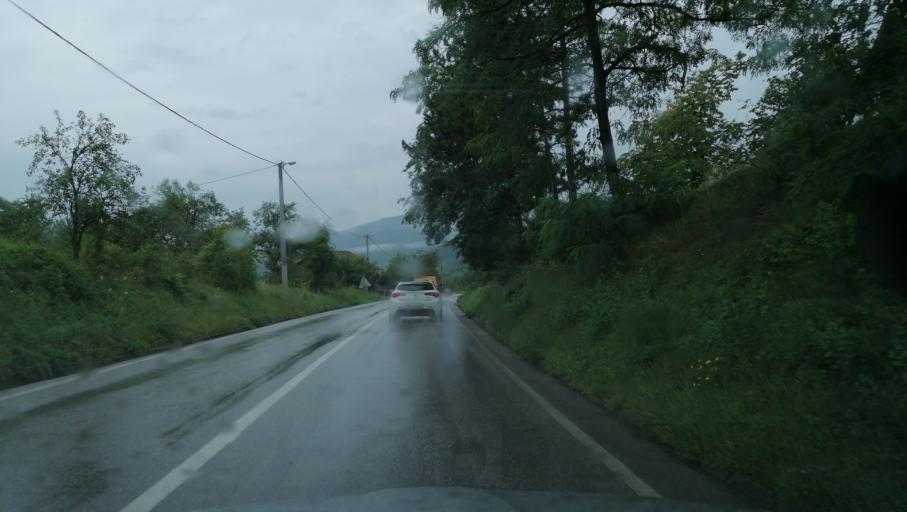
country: BA
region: Federation of Bosnia and Herzegovina
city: Gorazde
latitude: 43.6764
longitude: 19.0396
